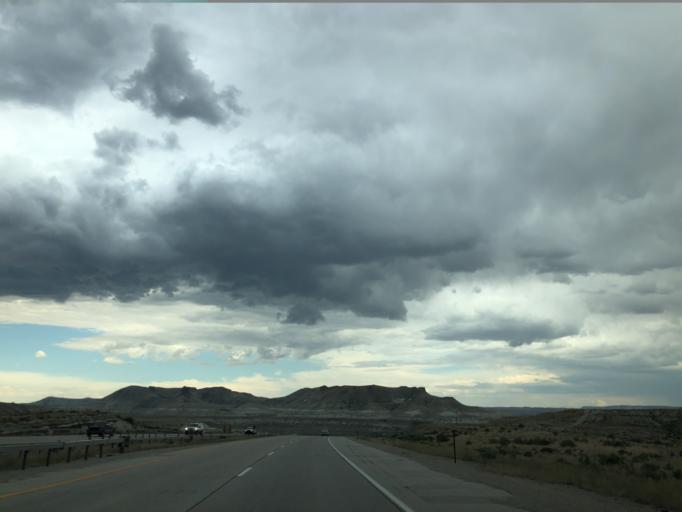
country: US
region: Wyoming
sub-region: Sweetwater County
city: Green River
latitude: 41.5312
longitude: -109.4591
